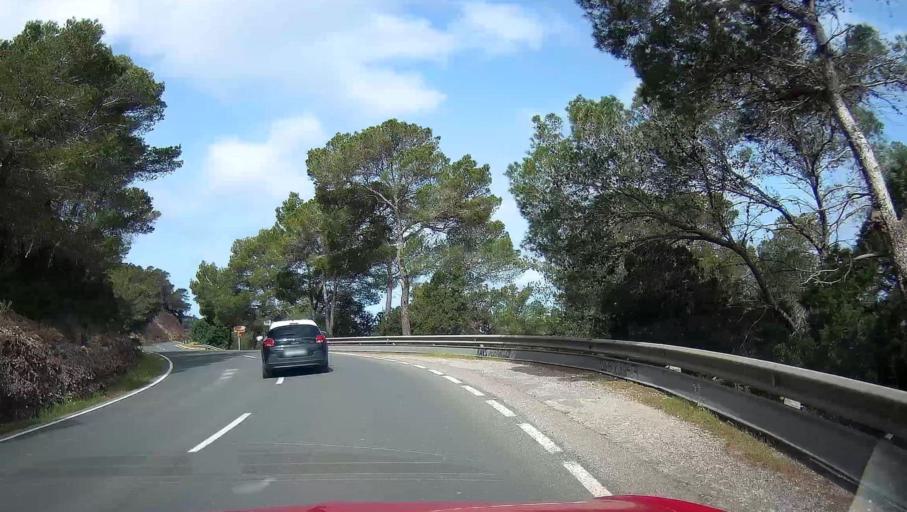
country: ES
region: Balearic Islands
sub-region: Illes Balears
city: Sant Joan de Labritja
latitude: 39.0996
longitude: 1.5045
